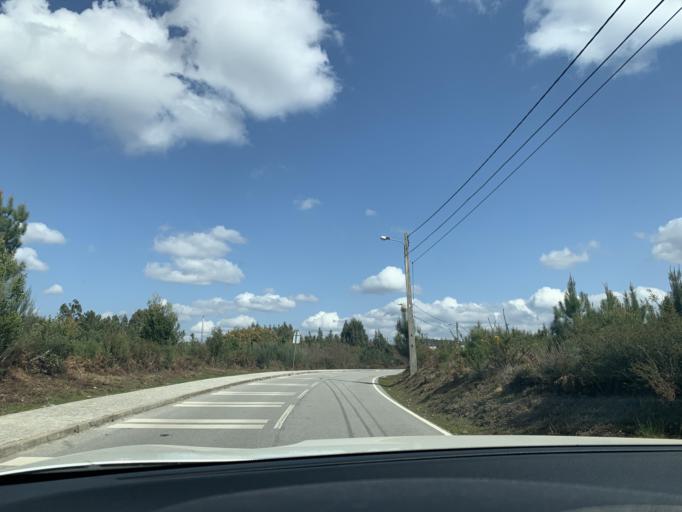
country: PT
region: Viseu
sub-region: Viseu
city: Rio de Loba
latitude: 40.6989
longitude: -7.8623
